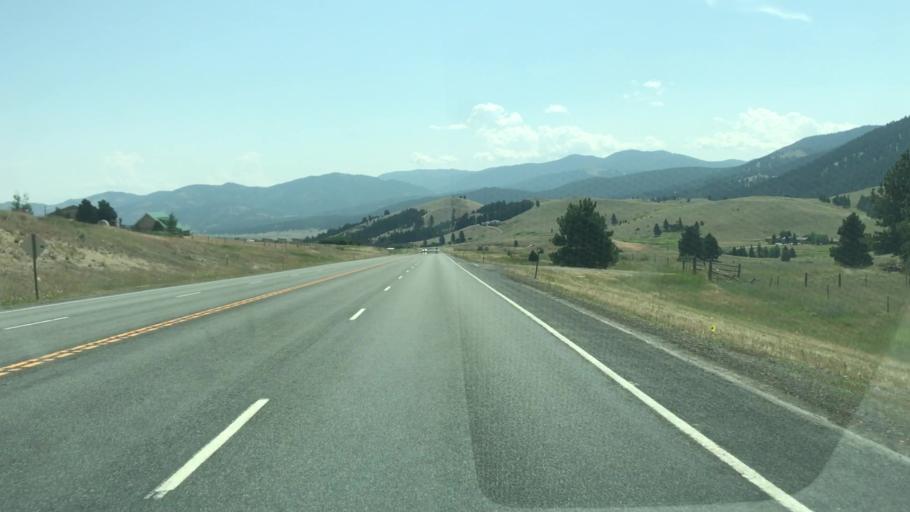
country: US
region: Montana
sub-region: Lewis and Clark County
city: Helena West Side
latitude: 46.5768
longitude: -112.2497
